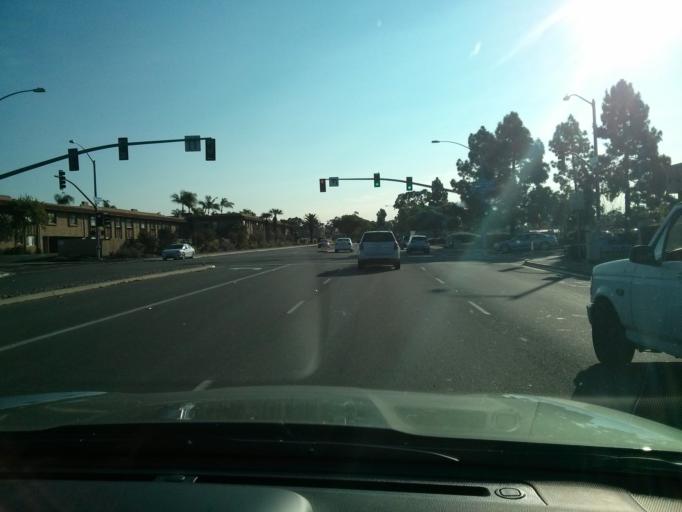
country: US
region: California
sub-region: San Diego County
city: La Jolla
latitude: 32.8203
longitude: -117.1722
